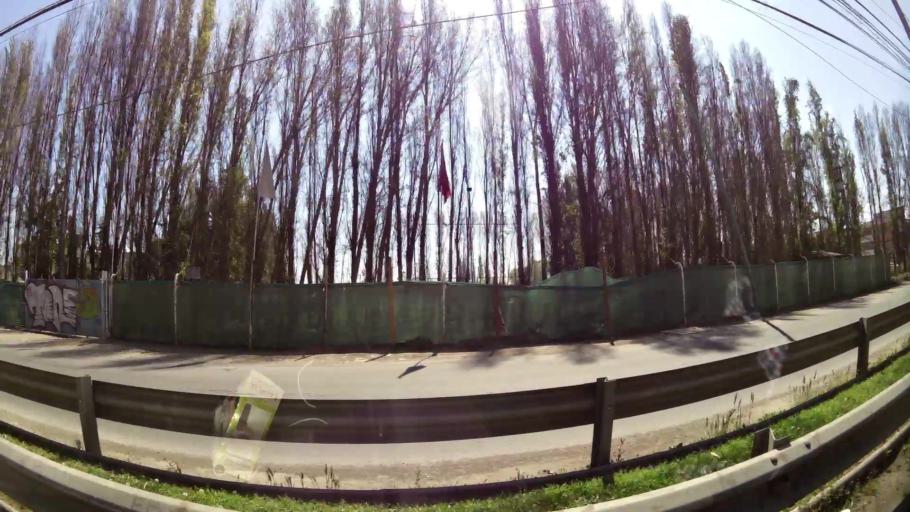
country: CL
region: Santiago Metropolitan
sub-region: Provincia de Santiago
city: Lo Prado
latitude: -33.3583
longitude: -70.7381
